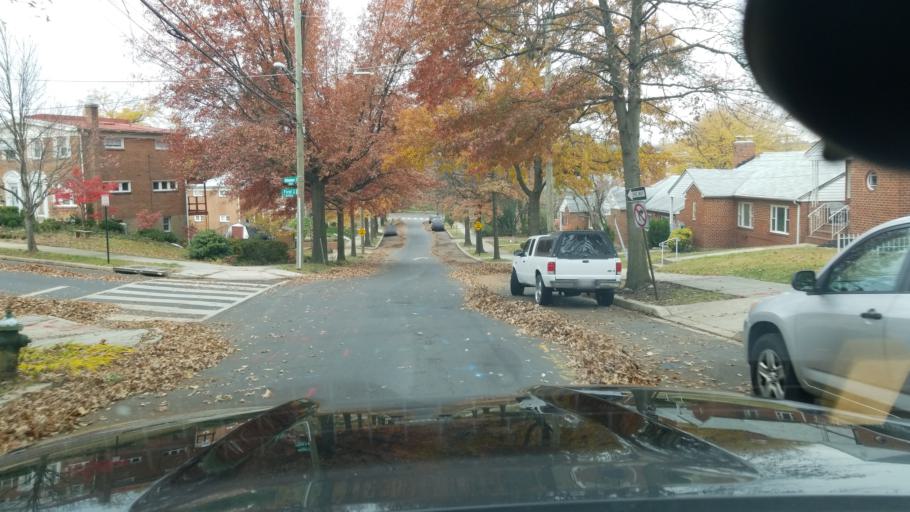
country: US
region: Maryland
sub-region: Montgomery County
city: Takoma Park
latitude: 38.9655
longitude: -77.0066
